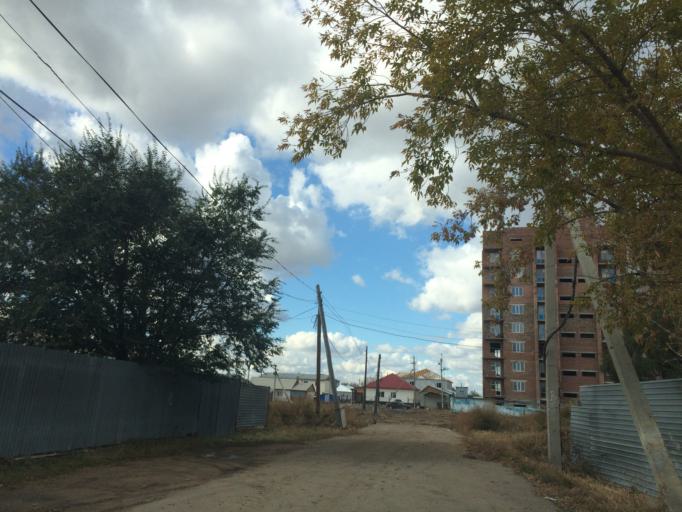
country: KZ
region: Astana Qalasy
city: Astana
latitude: 51.1867
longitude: 71.3818
